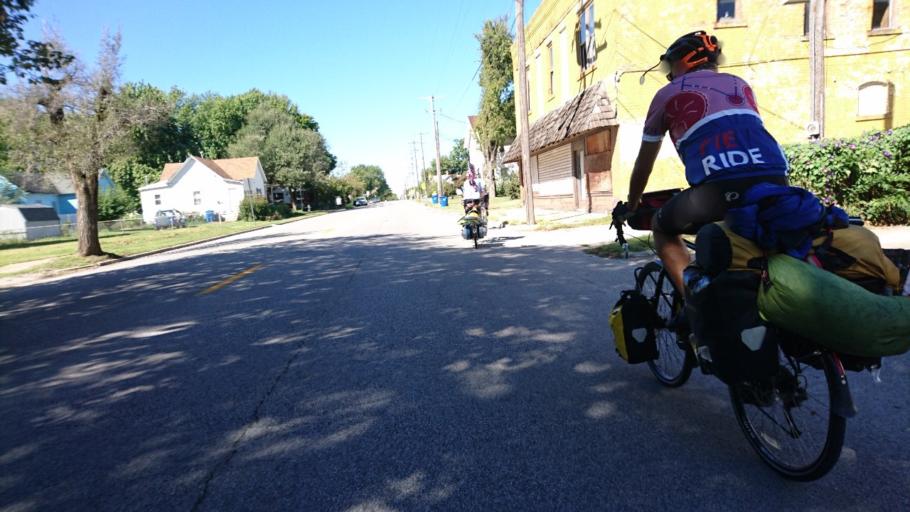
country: US
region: Missouri
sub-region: Jasper County
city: Joplin
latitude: 37.0900
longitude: -94.5216
